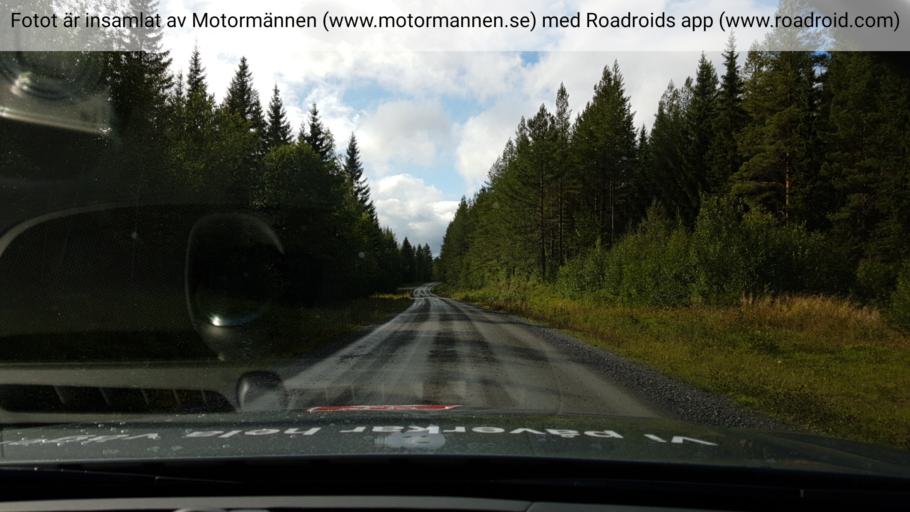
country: SE
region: Jaemtland
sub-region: Krokoms Kommun
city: Krokom
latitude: 63.7027
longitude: 14.5481
